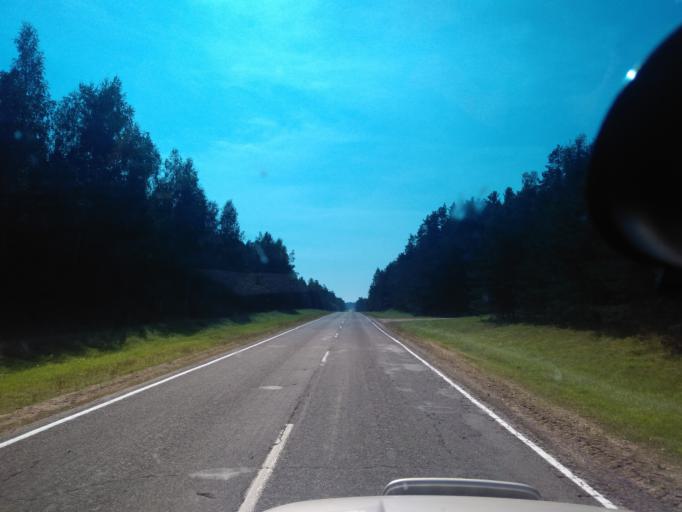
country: BY
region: Minsk
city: Uzda
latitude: 53.3247
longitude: 27.2320
